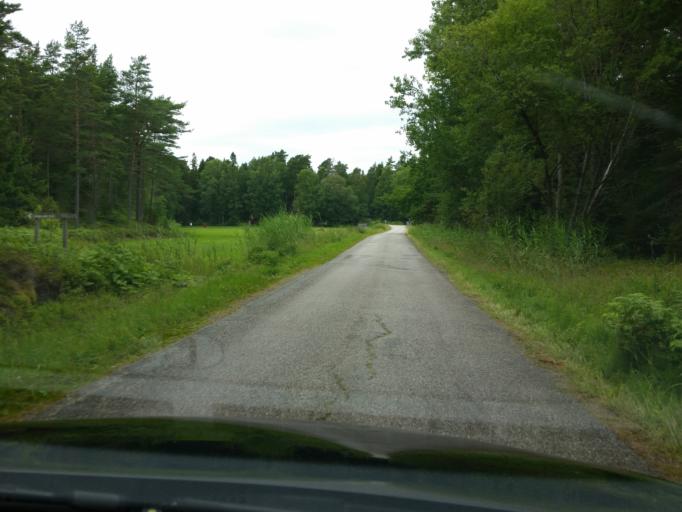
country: SE
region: Soedermanland
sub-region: Trosa Kommun
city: Trosa
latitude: 58.7468
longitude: 17.3828
